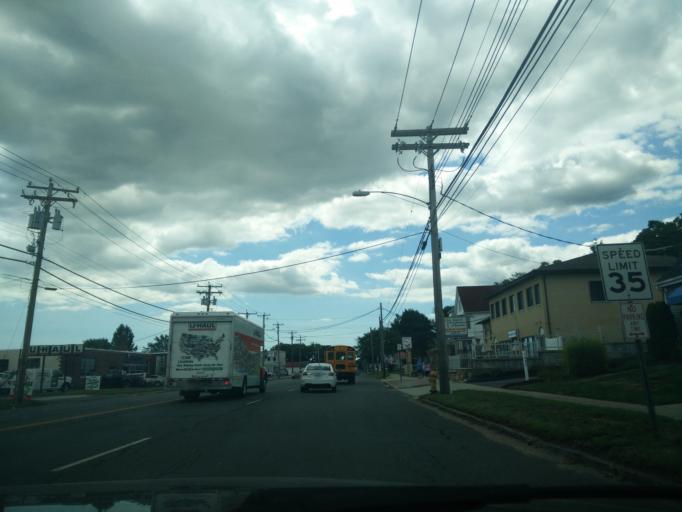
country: US
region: Connecticut
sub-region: New Haven County
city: Hamden
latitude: 41.3583
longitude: -72.9263
